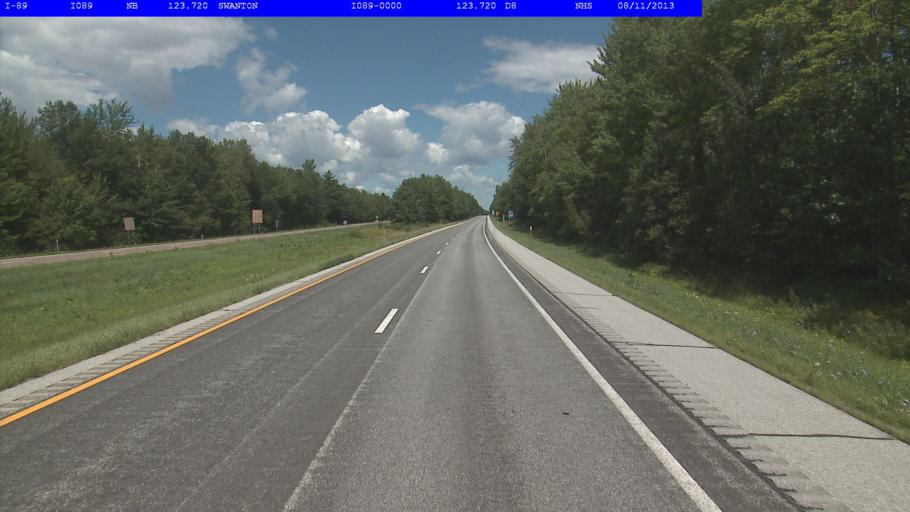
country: US
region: Vermont
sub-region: Franklin County
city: Swanton
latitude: 44.9271
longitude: -73.1098
